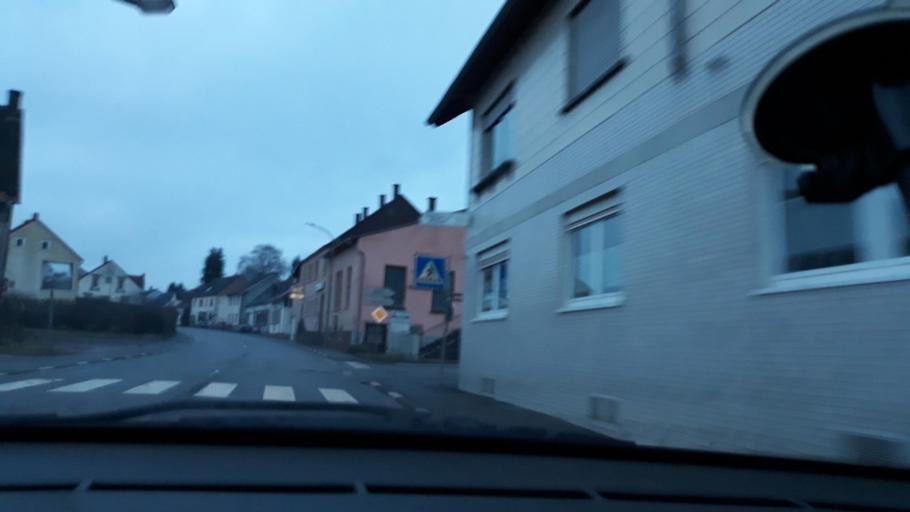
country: DE
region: Saarland
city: Blieskastel
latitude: 49.1984
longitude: 7.2454
